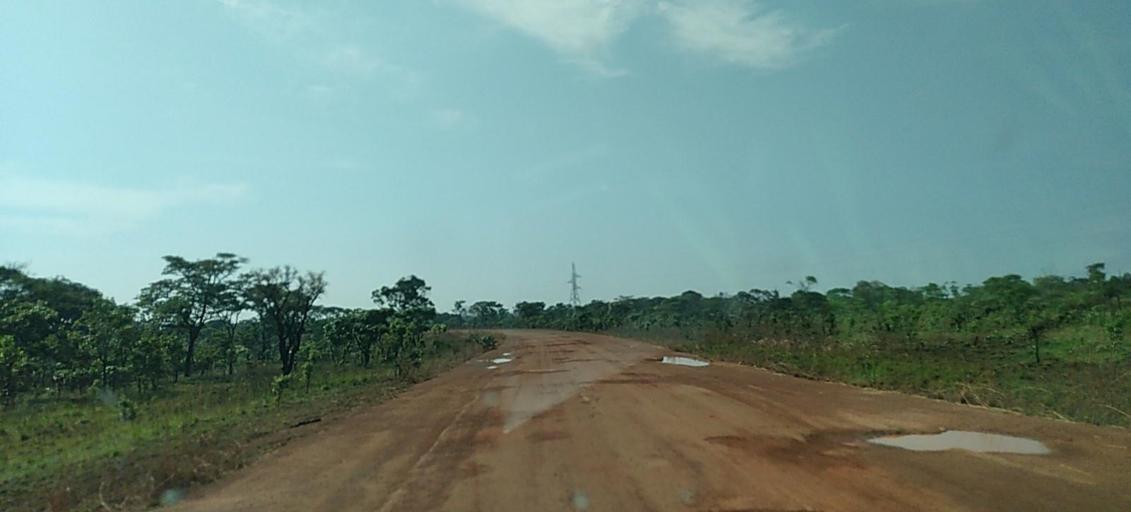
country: ZM
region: North-Western
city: Mwinilunga
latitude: -11.7845
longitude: 25.0259
